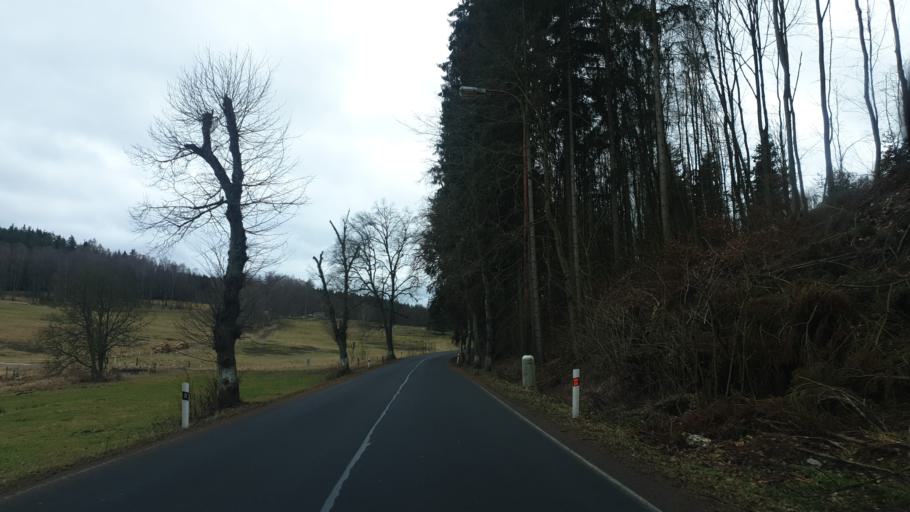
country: CZ
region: Karlovarsky
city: As
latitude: 50.2535
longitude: 12.2001
